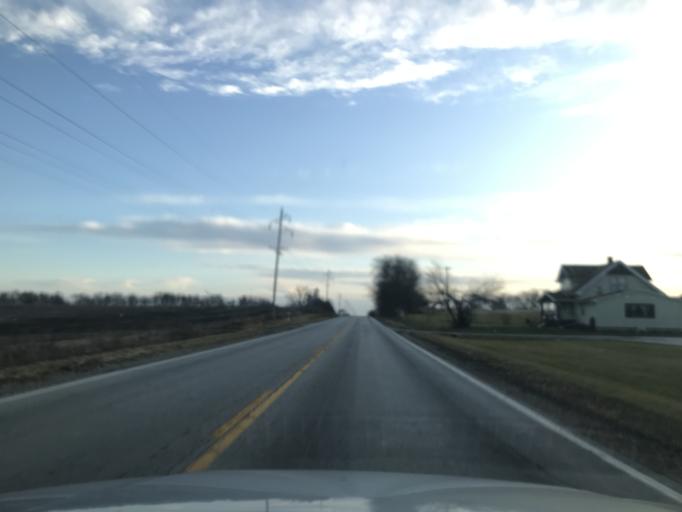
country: US
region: Illinois
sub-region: Mercer County
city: Aledo
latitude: 41.0419
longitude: -90.7459
